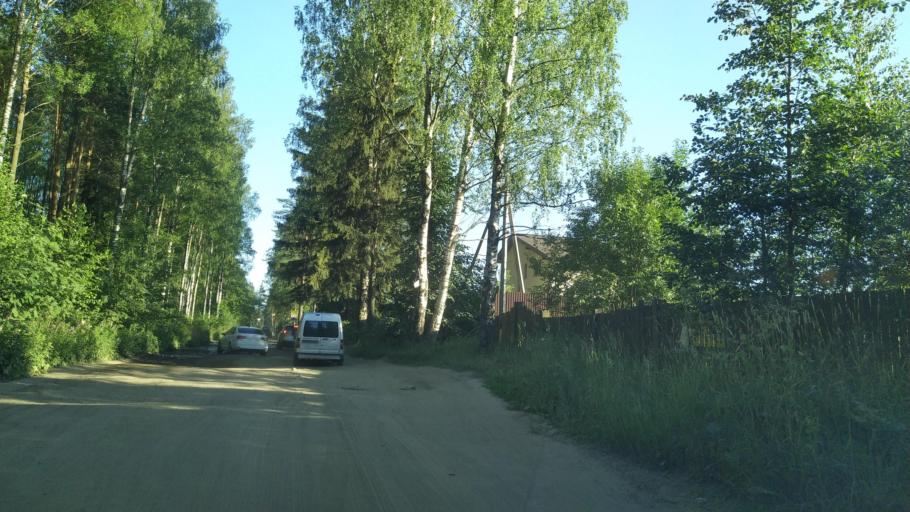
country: RU
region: Leningrad
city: Koltushi
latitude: 59.9152
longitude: 30.7349
